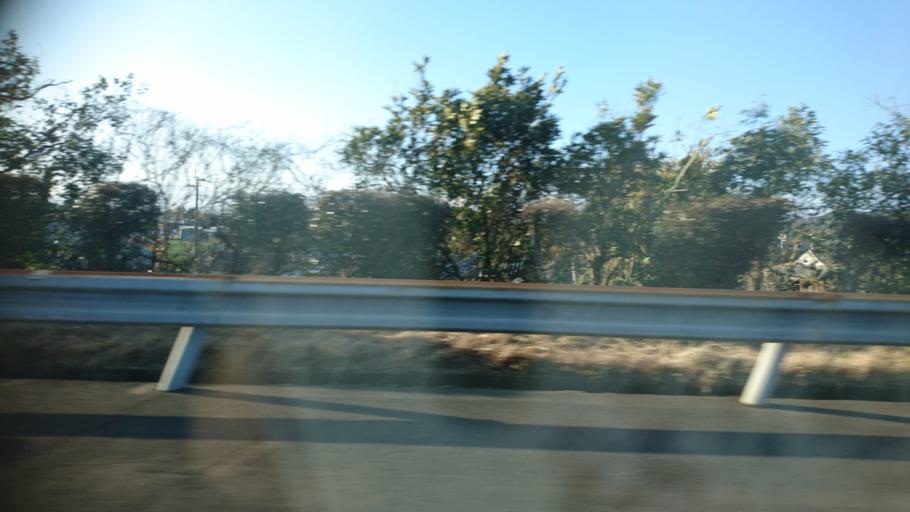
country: JP
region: Miyazaki
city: Miyakonojo
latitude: 31.7873
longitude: 131.1491
